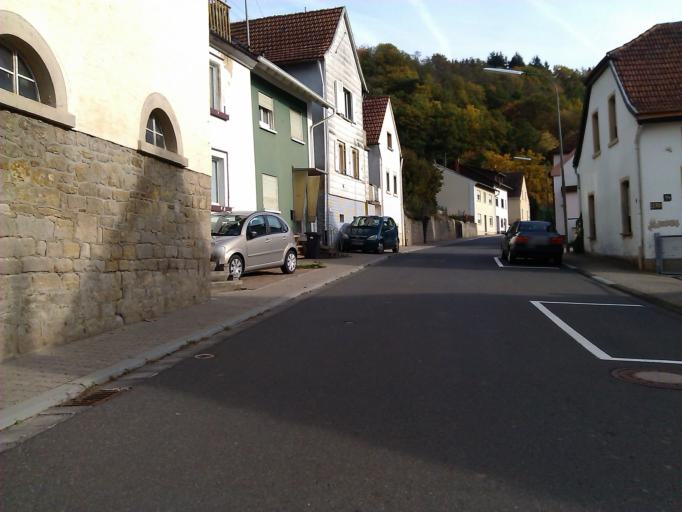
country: DE
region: Rheinland-Pfalz
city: Odenbach
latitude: 49.6822
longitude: 7.6533
